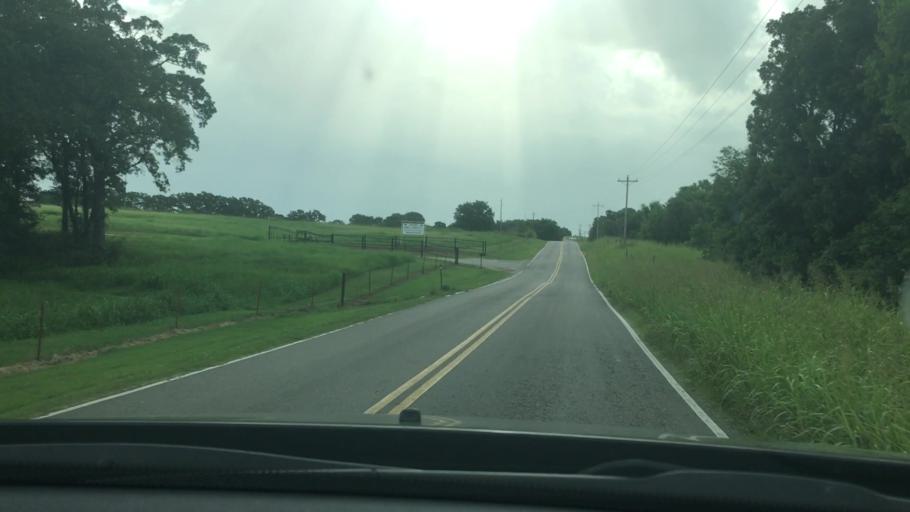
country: US
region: Oklahoma
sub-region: Pontotoc County
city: Ada
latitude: 34.8105
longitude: -96.6236
